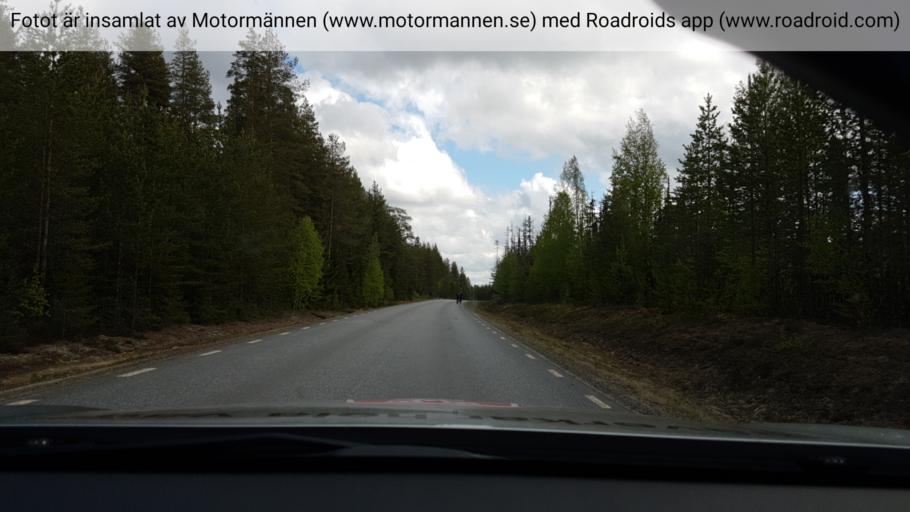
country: SE
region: Vaesterbotten
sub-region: Vindelns Kommun
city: Vindeln
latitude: 64.1794
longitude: 19.6614
